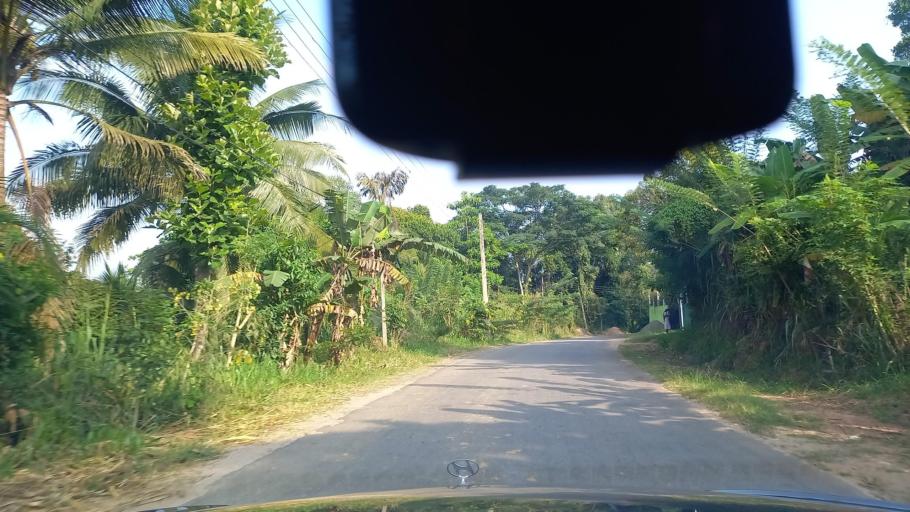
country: LK
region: Central
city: Gampola
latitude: 7.2208
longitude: 80.6059
